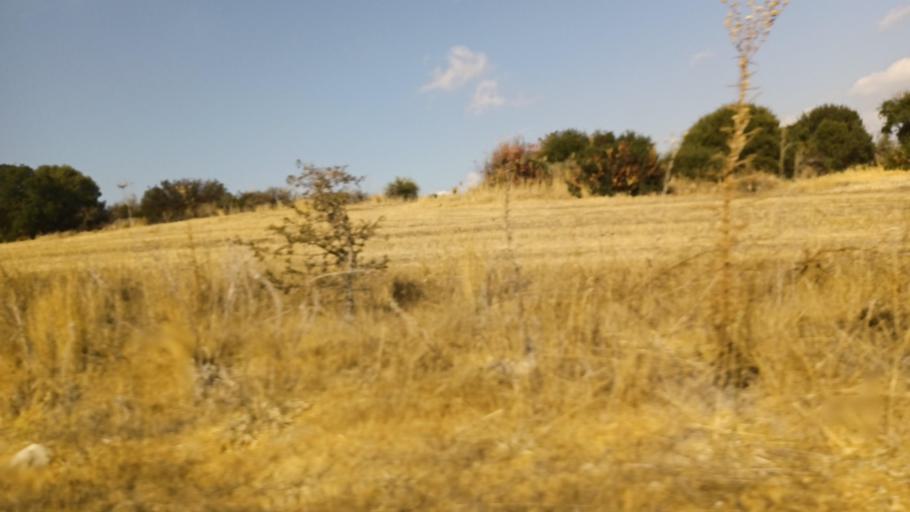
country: CY
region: Pafos
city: Polis
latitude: 34.9776
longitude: 32.4302
